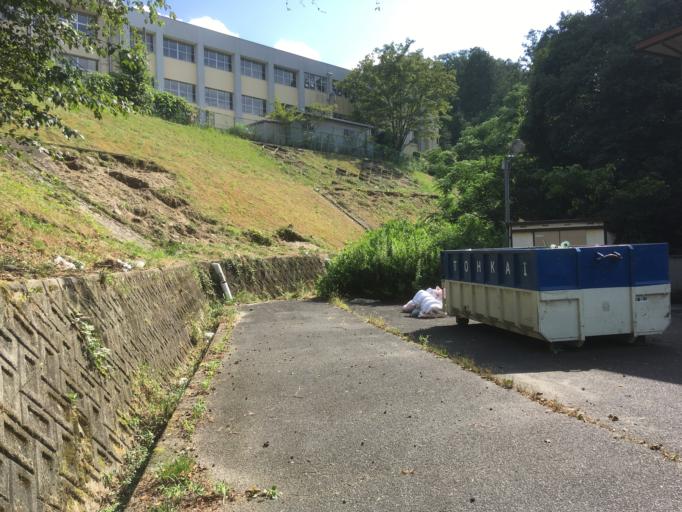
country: JP
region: Nara
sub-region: Ikoma-shi
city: Ikoma
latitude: 34.7068
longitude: 135.6891
